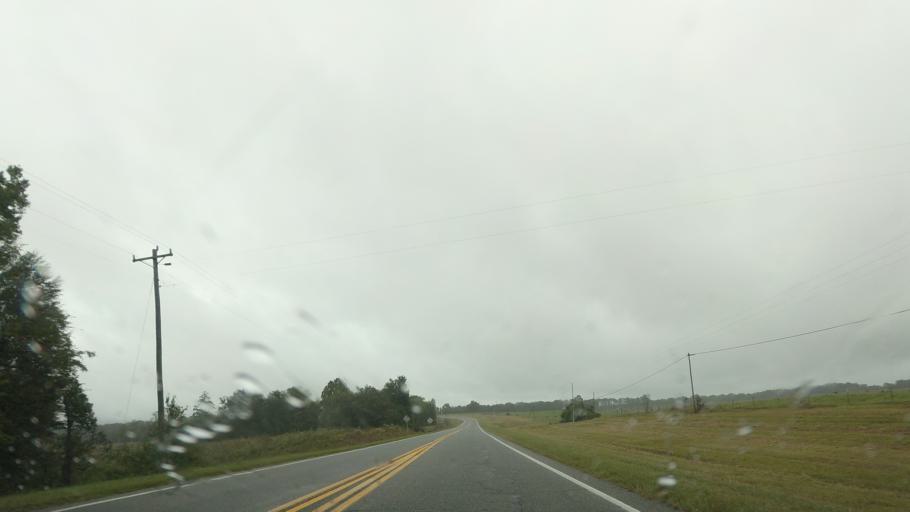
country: US
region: Georgia
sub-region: Ben Hill County
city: Fitzgerald
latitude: 31.7697
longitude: -83.2445
